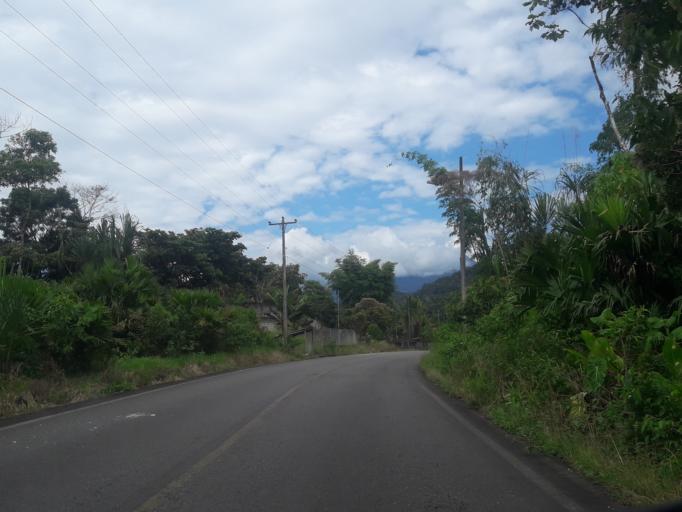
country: EC
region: Napo
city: Tena
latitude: -1.0388
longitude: -77.8941
